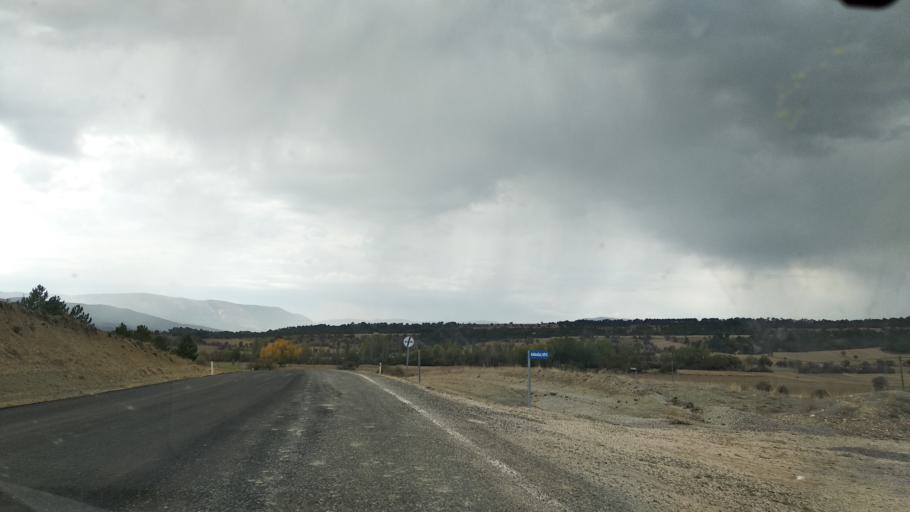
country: TR
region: Bolu
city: Seben
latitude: 40.3503
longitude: 31.4768
